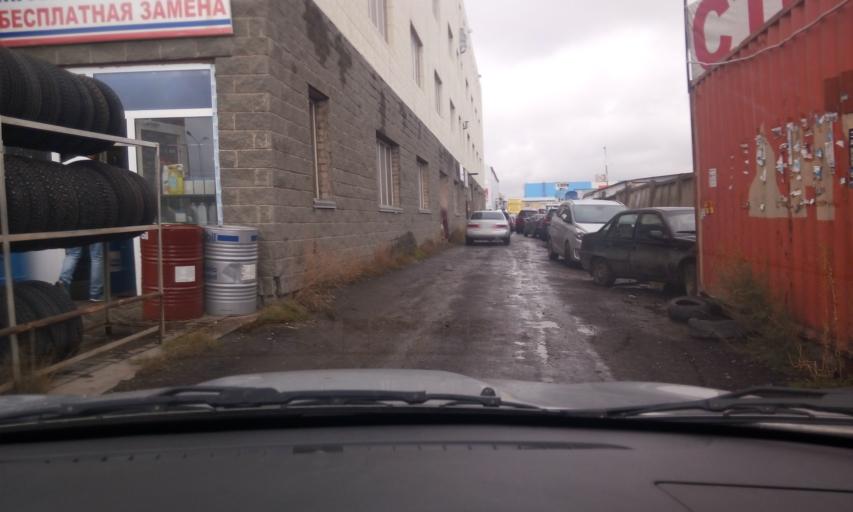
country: KZ
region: Astana Qalasy
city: Astana
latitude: 51.1802
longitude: 71.3810
